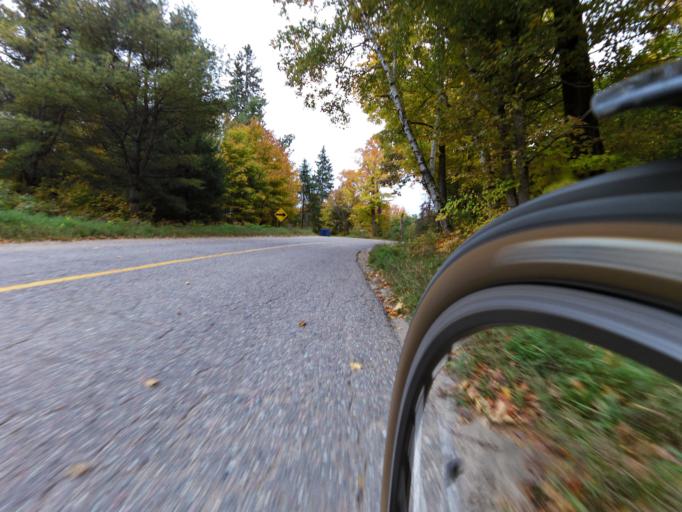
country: CA
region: Quebec
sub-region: Outaouais
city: Wakefield
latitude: 45.6721
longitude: -76.0096
